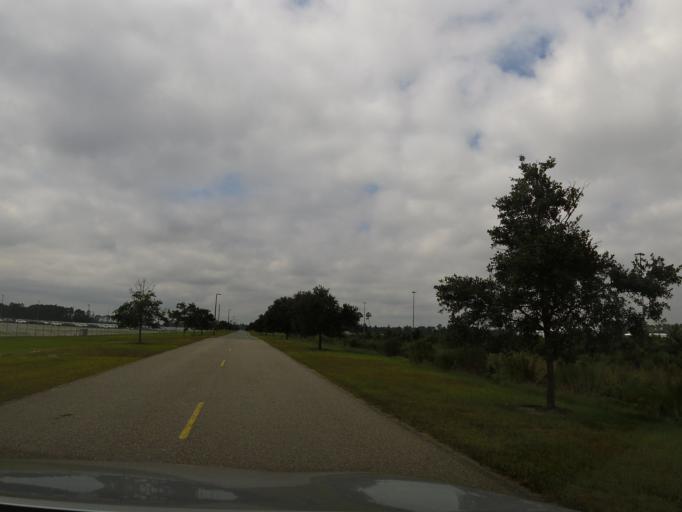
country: US
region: Georgia
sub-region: Glynn County
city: Brunswick
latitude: 31.1071
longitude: -81.5383
